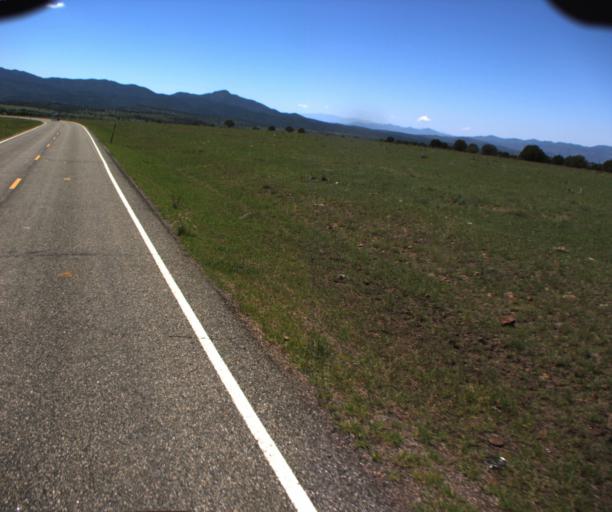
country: US
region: Arizona
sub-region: Greenlee County
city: Morenci
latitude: 33.3254
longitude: -109.3512
